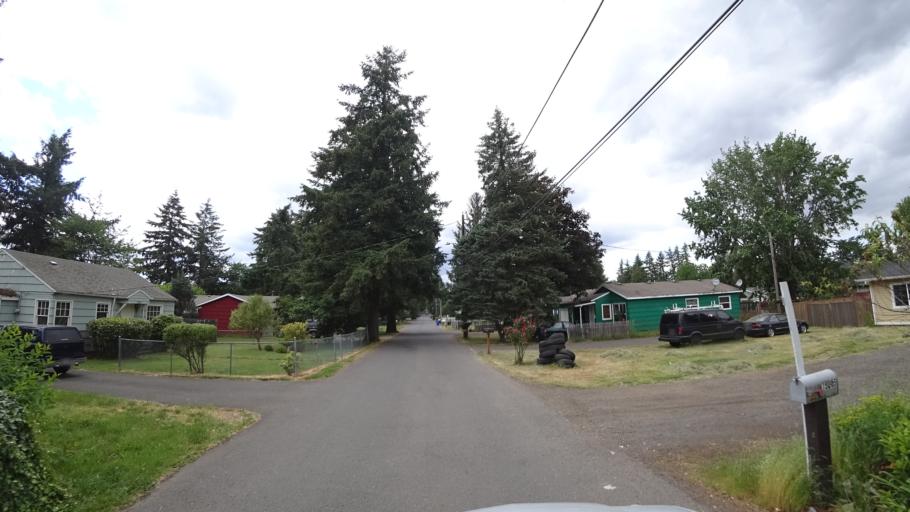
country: US
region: Oregon
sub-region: Multnomah County
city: Lents
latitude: 45.4960
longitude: -122.5199
